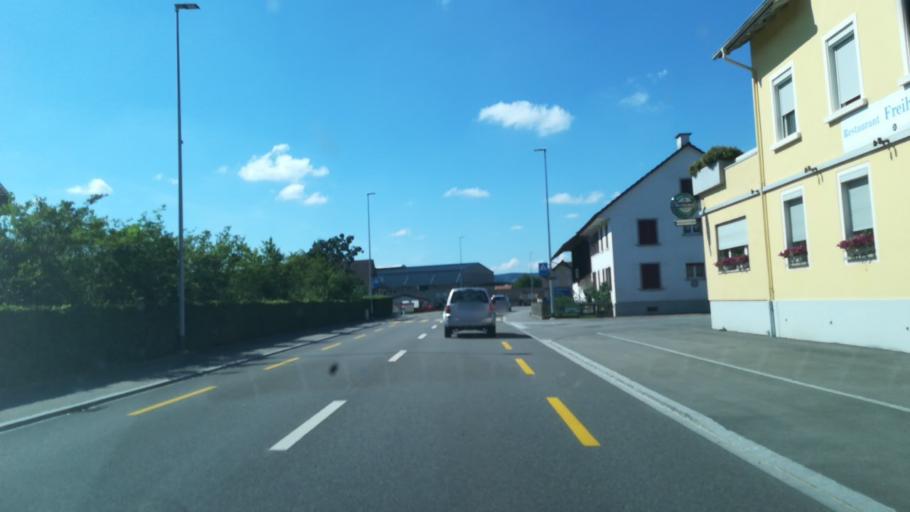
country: CH
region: Thurgau
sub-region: Weinfelden District
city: Sulgen
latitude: 47.5331
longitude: 9.1881
